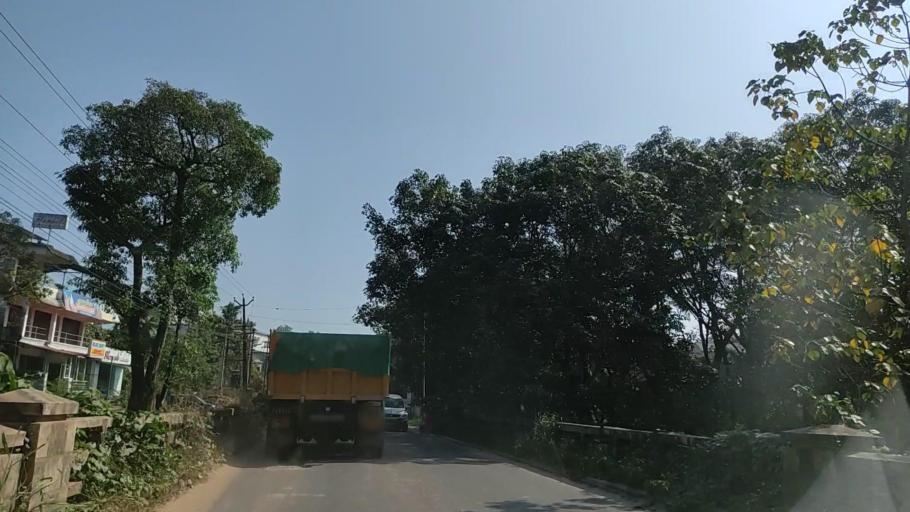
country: IN
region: Kerala
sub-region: Kollam
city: Punalur
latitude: 8.9258
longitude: 76.9034
